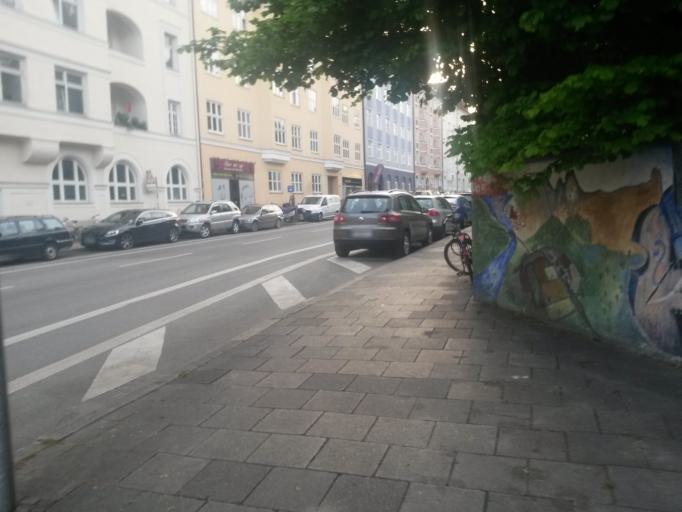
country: DE
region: Bavaria
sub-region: Upper Bavaria
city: Munich
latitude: 48.1271
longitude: 11.5825
